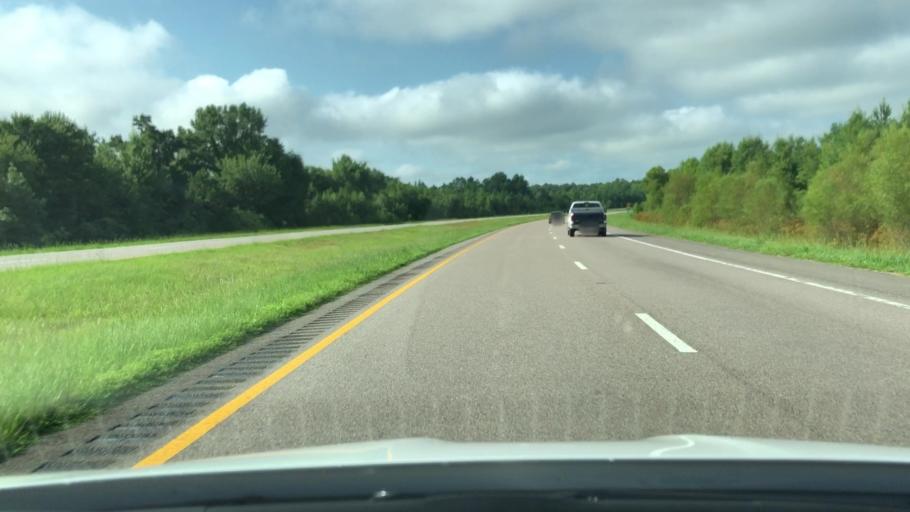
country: US
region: Virginia
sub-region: City of Portsmouth
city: Portsmouth Heights
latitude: 36.6540
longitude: -76.3544
